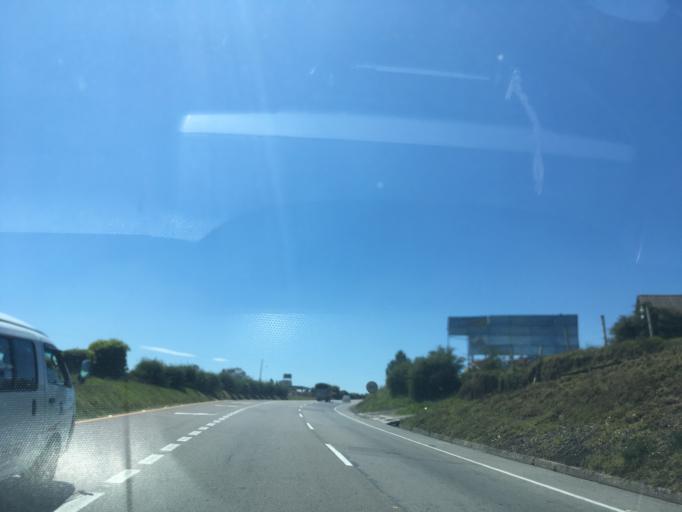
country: CO
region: Boyaca
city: Tuta
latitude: 5.6943
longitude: -73.2501
